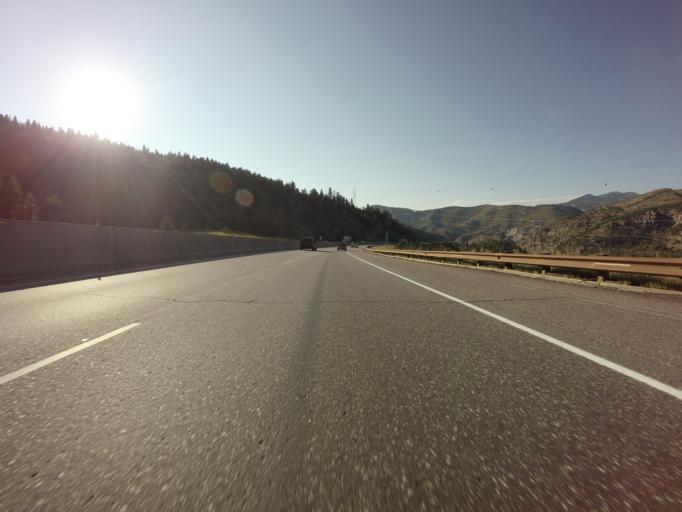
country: US
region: Colorado
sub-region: Clear Creek County
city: Idaho Springs
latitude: 39.7294
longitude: -105.4249
